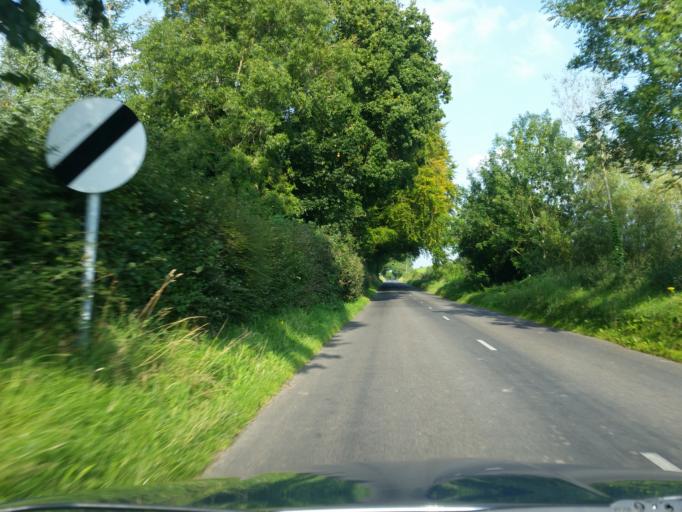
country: GB
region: Northern Ireland
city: Ballinamallard
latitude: 54.3190
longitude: -7.5304
